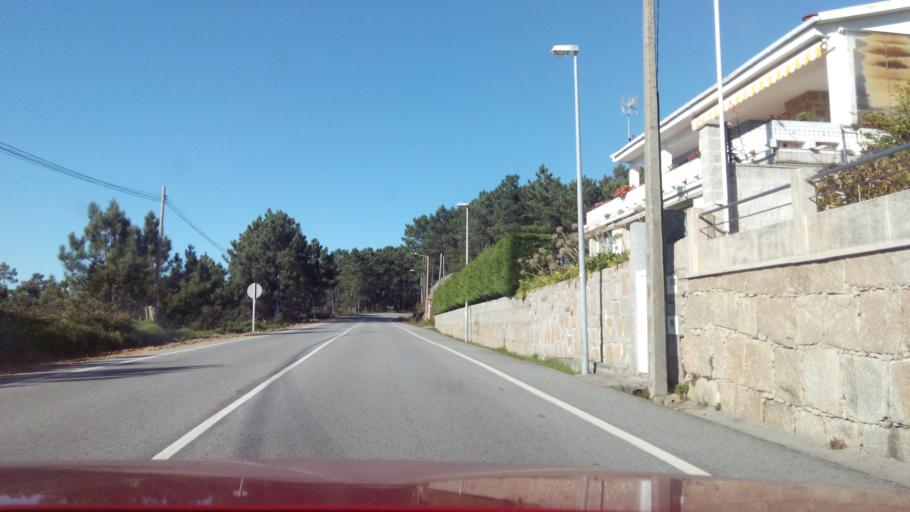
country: ES
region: Galicia
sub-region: Provincia de Pontevedra
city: O Grove
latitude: 42.4569
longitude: -8.9265
